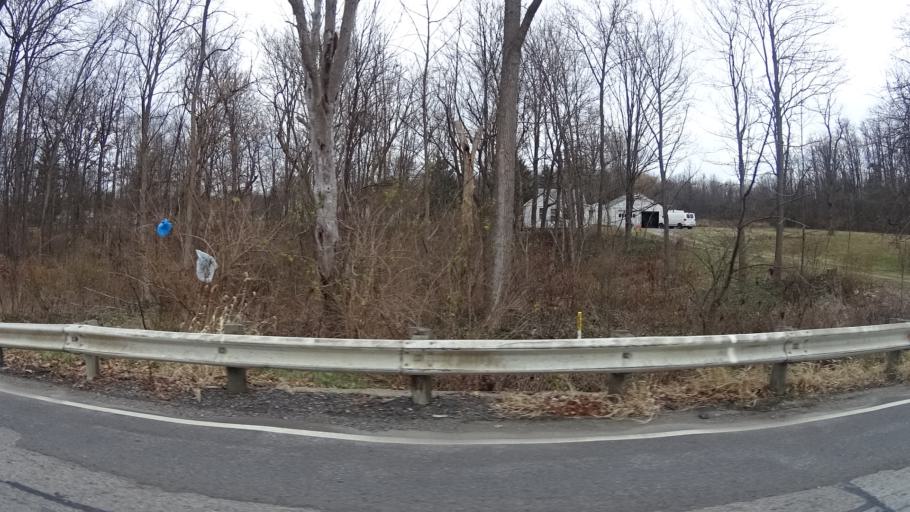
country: US
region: Ohio
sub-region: Cuyahoga County
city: Olmsted Falls
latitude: 41.3508
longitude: -81.8922
